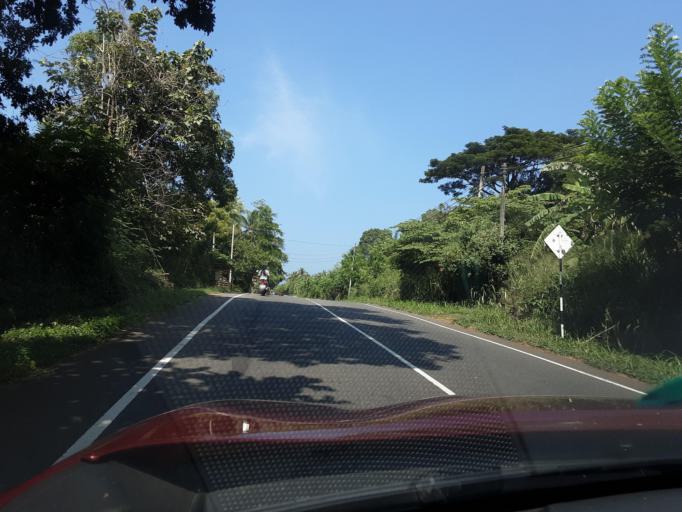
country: LK
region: Uva
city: Badulla
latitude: 7.1879
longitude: 81.0374
